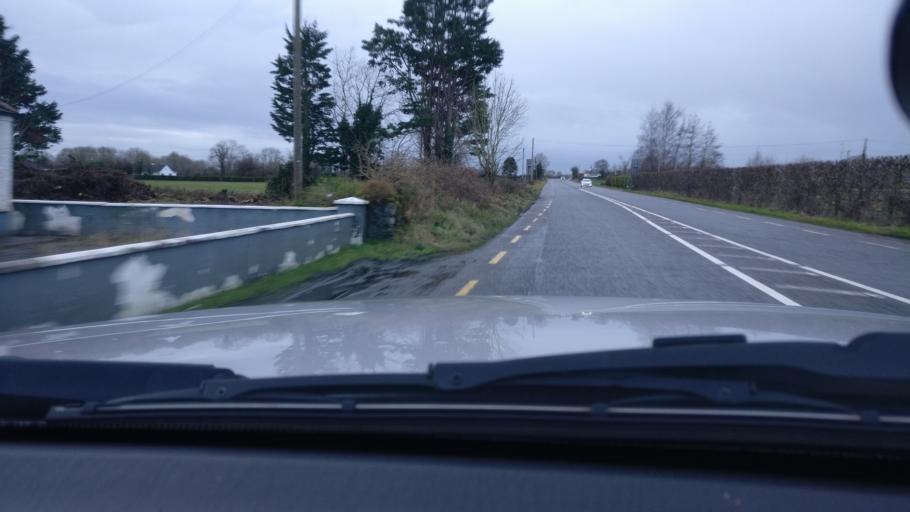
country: IE
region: Leinster
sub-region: An Iarmhi
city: Athlone
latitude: 53.3689
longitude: -8.0288
